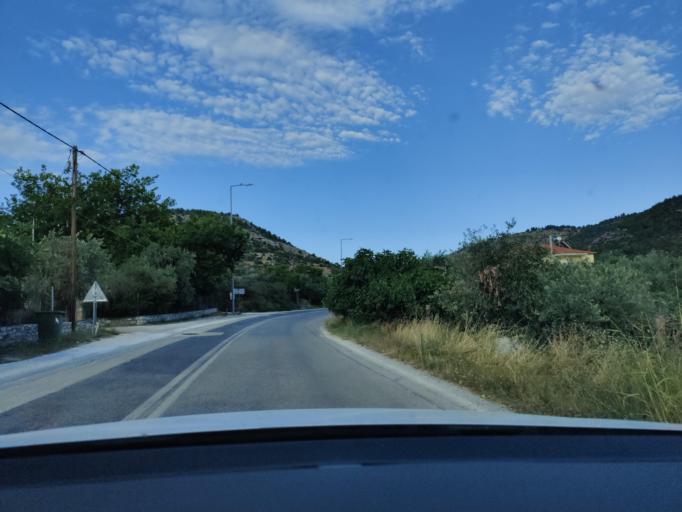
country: GR
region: East Macedonia and Thrace
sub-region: Nomos Kavalas
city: Limenaria
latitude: 40.6135
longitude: 24.6228
